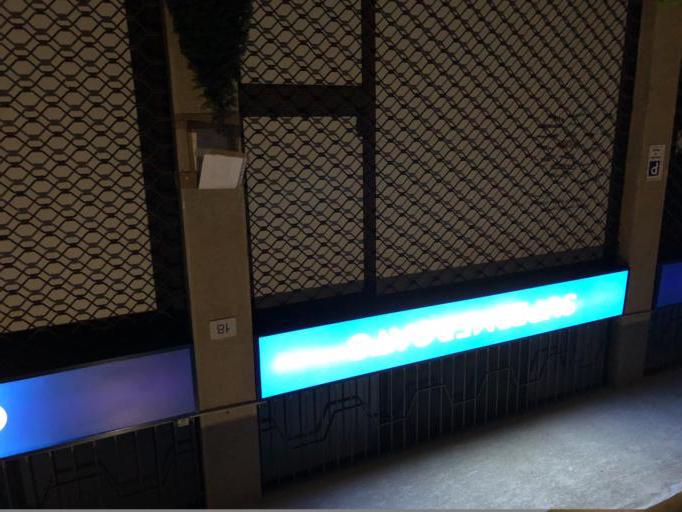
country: IT
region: Lombardy
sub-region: Provincia di Monza e Brianza
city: Aicurzio
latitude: 45.6397
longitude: 9.4163
